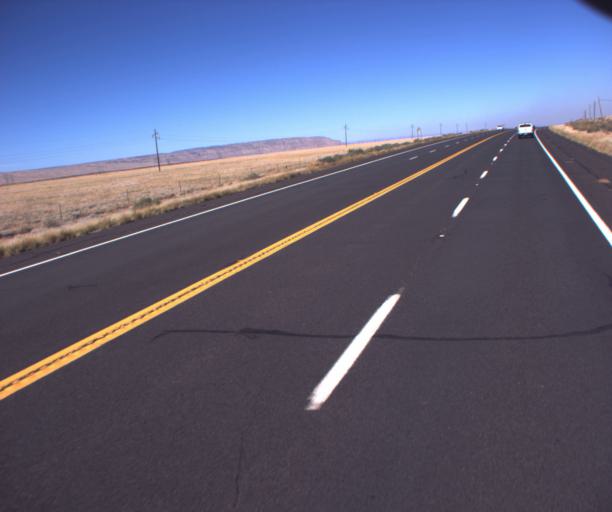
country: US
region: Arizona
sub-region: Coconino County
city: Flagstaff
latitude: 35.6469
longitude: -111.5168
